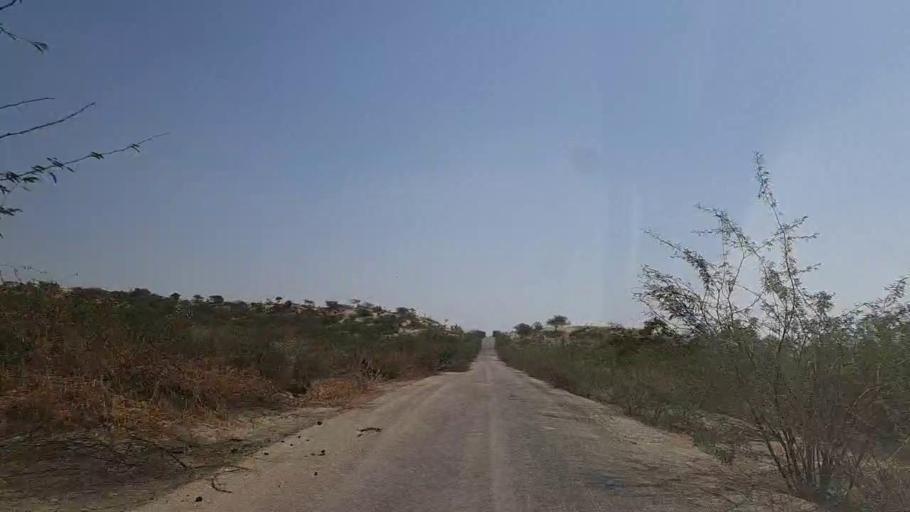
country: PK
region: Sindh
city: Diplo
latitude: 24.4917
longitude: 69.4370
